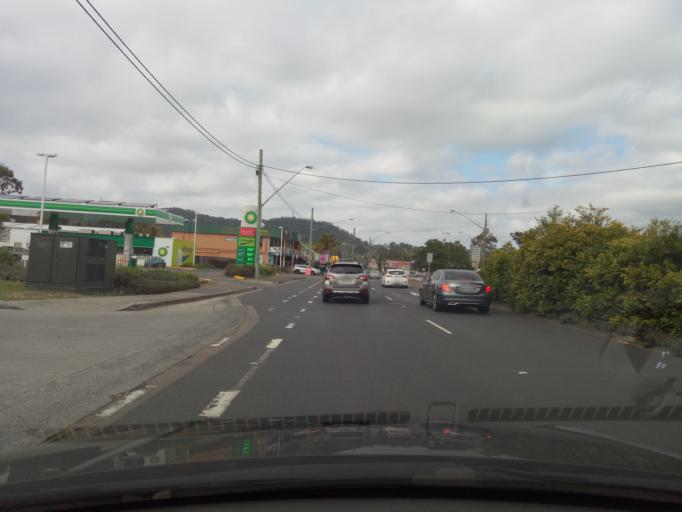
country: AU
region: New South Wales
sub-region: Gosford Shire
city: Narara
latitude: -33.4075
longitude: 151.3509
